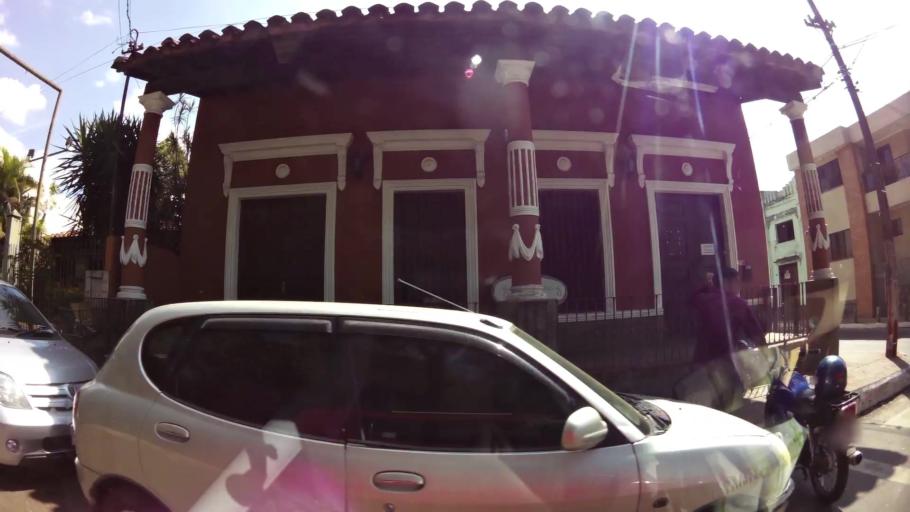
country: PY
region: Central
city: San Lorenzo
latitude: -25.3413
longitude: -57.5095
